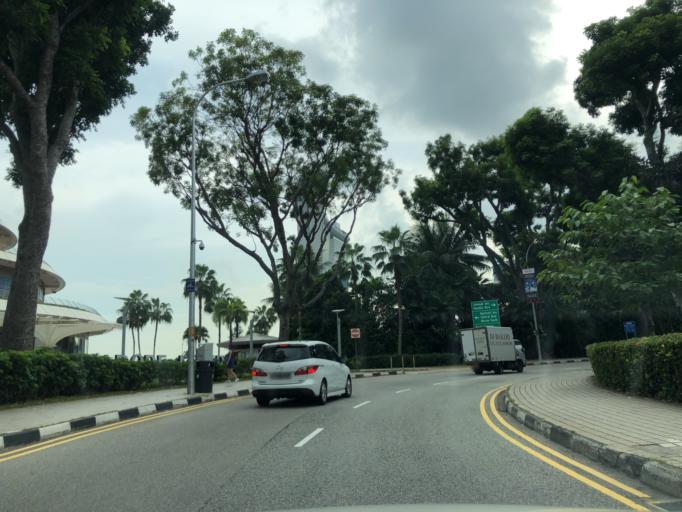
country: SG
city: Singapore
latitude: 1.2898
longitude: 103.8626
